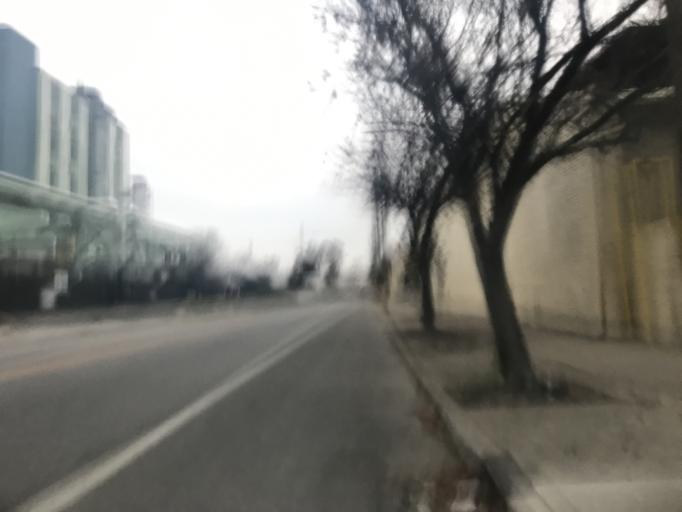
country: US
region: Kentucky
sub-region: Jefferson County
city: Louisville
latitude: 38.2340
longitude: -85.7741
